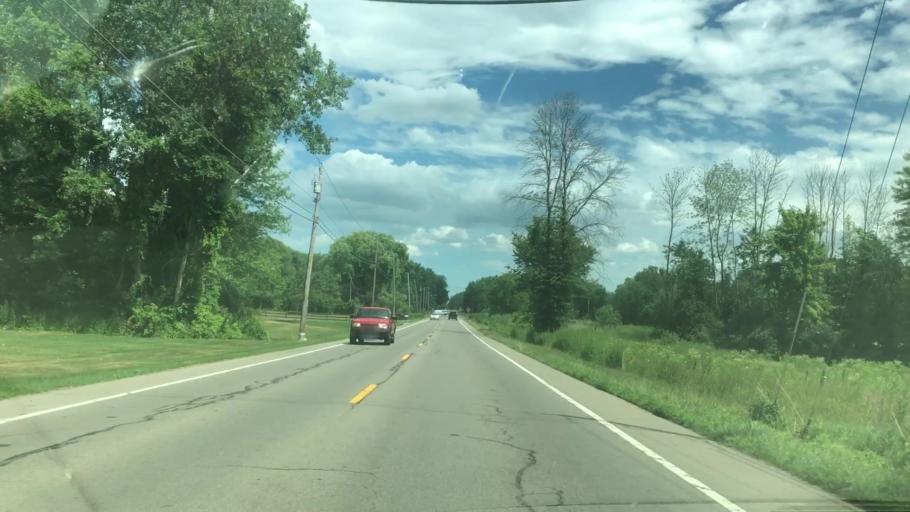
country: US
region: New York
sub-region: Monroe County
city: Webster
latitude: 43.1598
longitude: -77.4167
